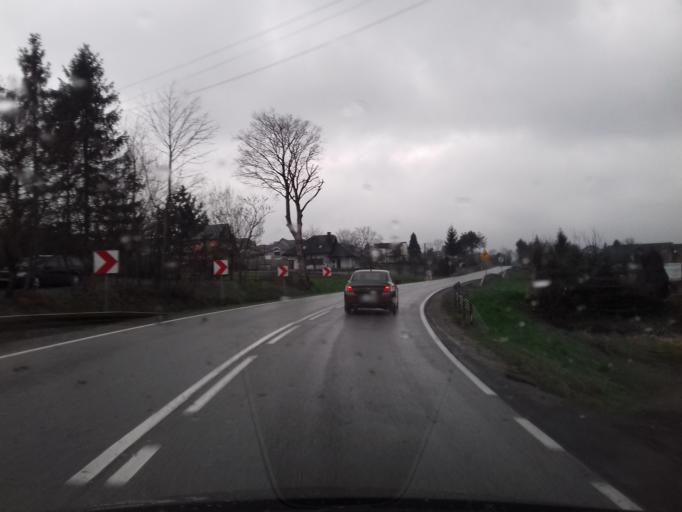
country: PL
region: Lesser Poland Voivodeship
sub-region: Powiat nowosadecki
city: Chelmiec
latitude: 49.6328
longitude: 20.6394
